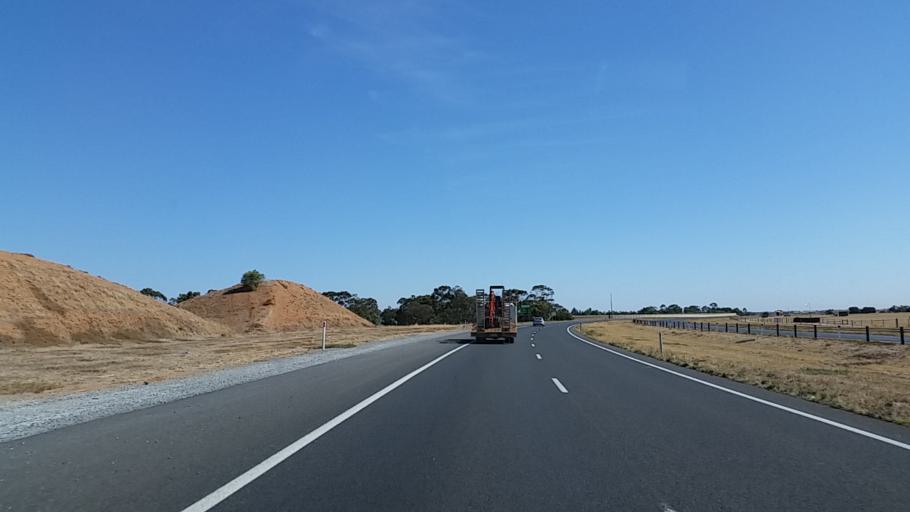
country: AU
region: South Australia
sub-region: Gawler
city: Gawler
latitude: -34.6015
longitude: 138.7230
